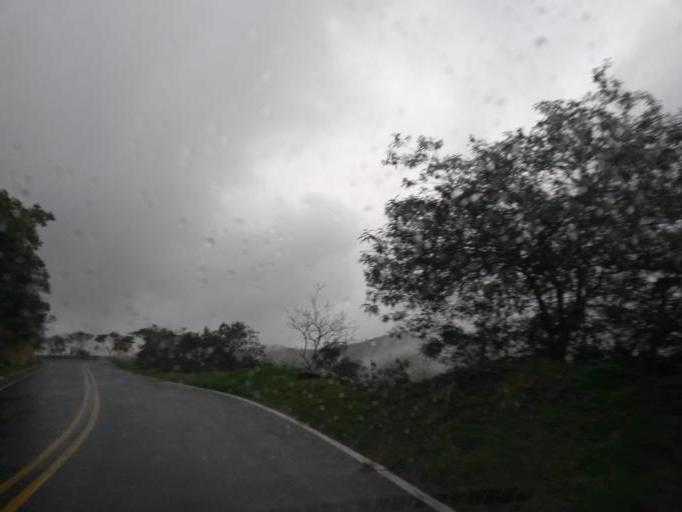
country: CO
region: Cauca
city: Popayan
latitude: 2.4050
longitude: -76.5053
